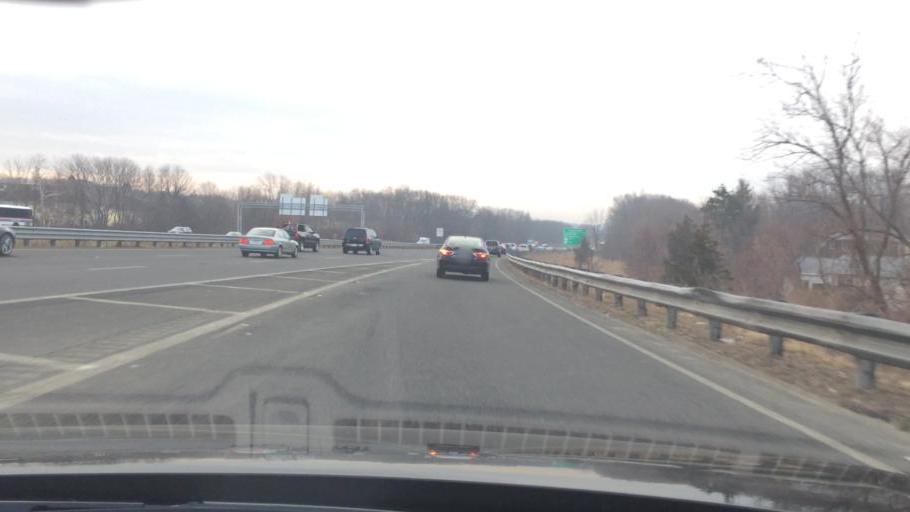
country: US
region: Massachusetts
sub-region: Essex County
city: North Andover
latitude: 42.7248
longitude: -71.1383
